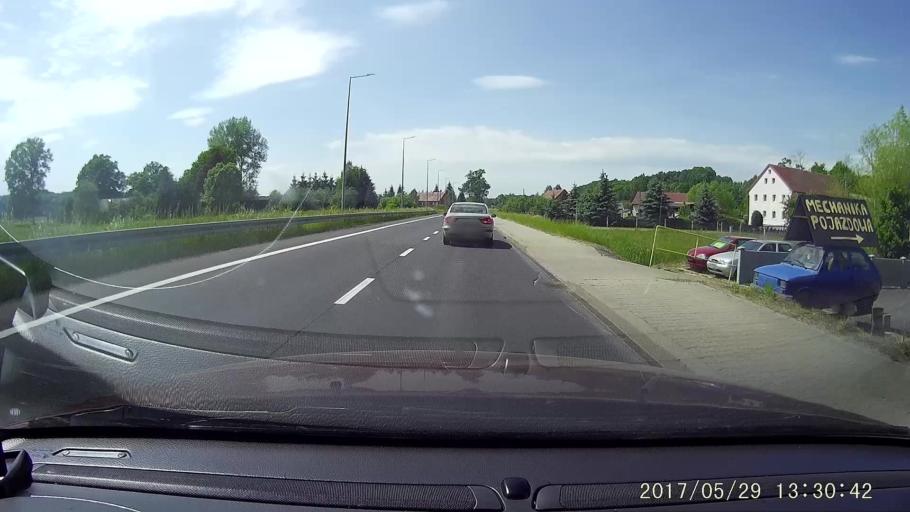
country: PL
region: Lower Silesian Voivodeship
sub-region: Powiat lubanski
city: Olszyna
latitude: 51.0767
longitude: 15.3521
